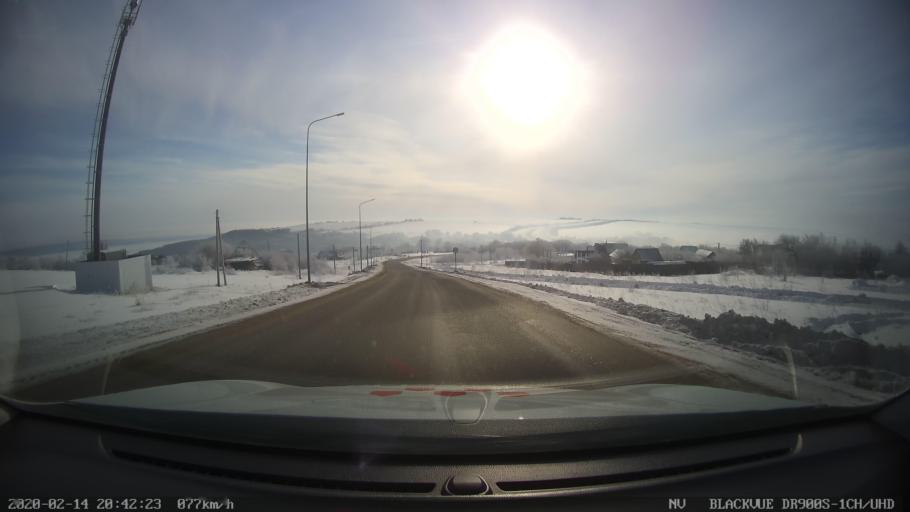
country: RU
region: Tatarstan
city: Kuybyshevskiy Zaton
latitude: 55.3175
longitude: 49.1418
